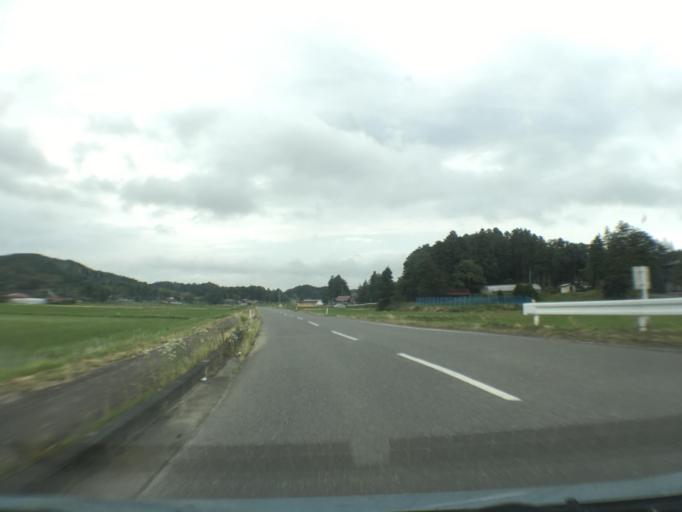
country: JP
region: Iwate
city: Ichinoseki
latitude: 38.7562
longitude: 141.2383
